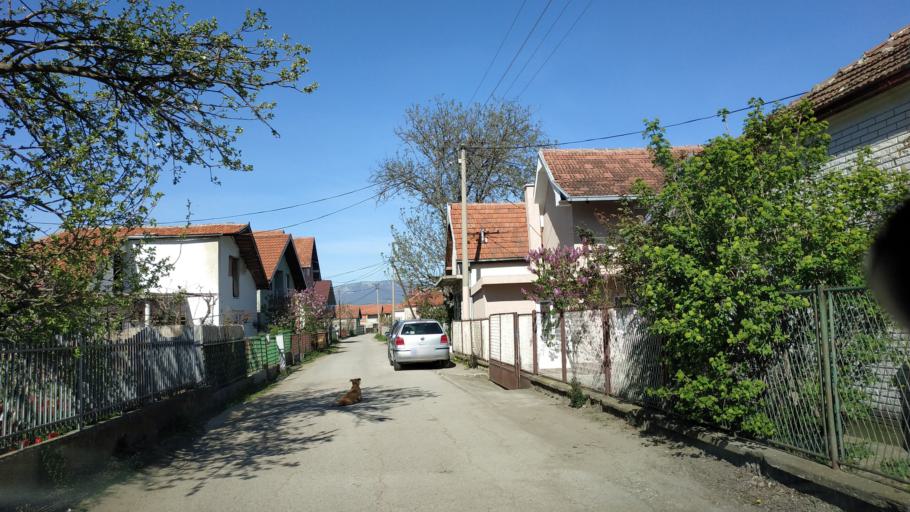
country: RS
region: Central Serbia
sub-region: Nisavski Okrug
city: Aleksinac
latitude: 43.4996
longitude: 21.6974
